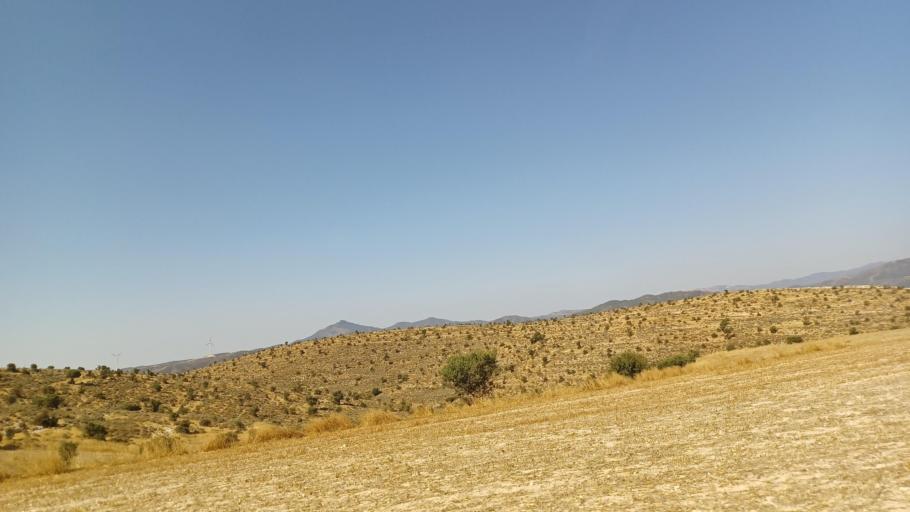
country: CY
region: Larnaka
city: Psevdas
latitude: 34.9711
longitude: 33.4823
